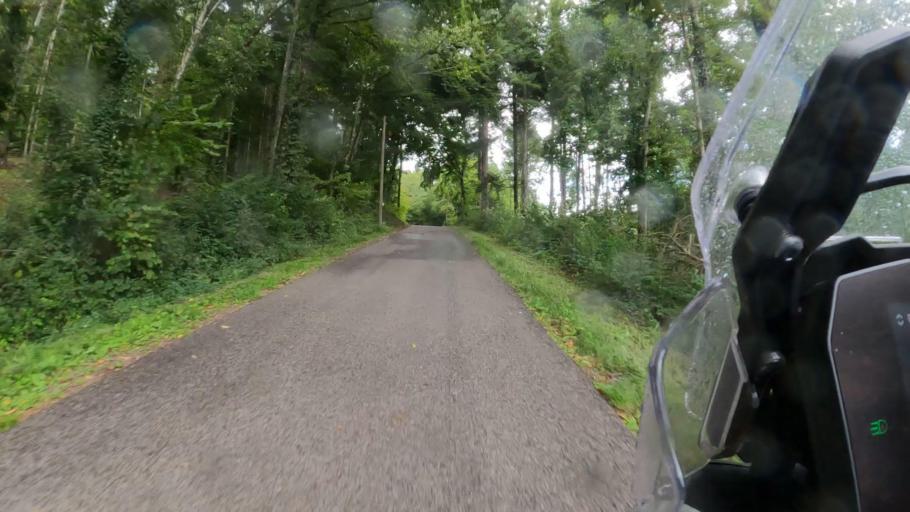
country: DE
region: Baden-Wuerttemberg
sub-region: Freiburg Region
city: Eggingen
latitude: 47.6711
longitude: 8.4000
